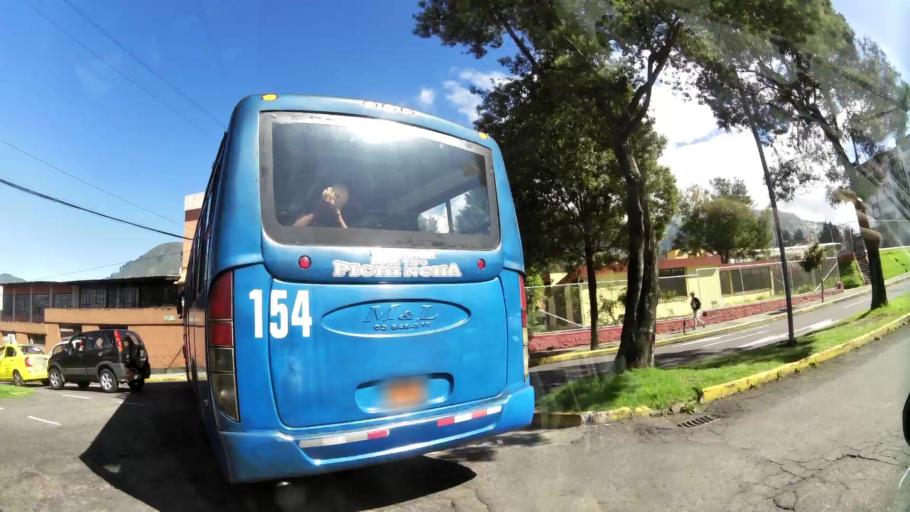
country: EC
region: Pichincha
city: Quito
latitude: -0.2388
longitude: -78.5259
